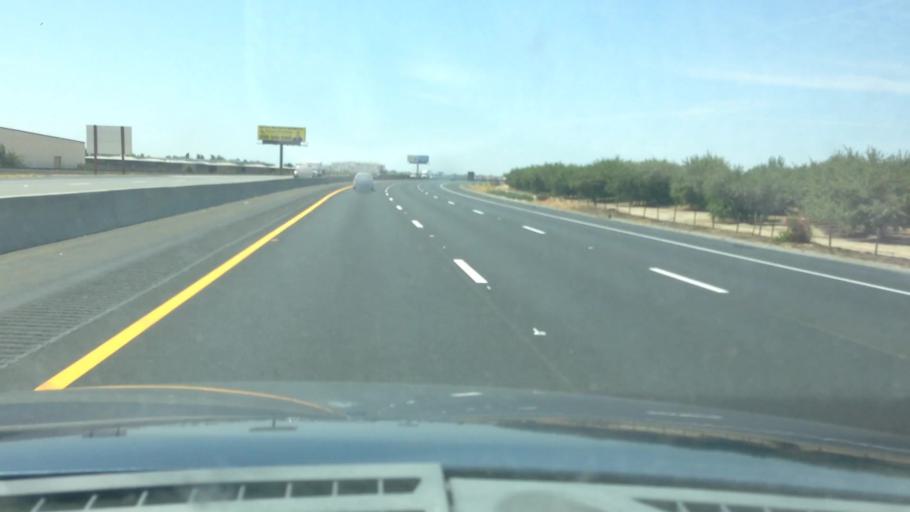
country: US
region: California
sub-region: Kern County
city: McFarland
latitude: 35.7151
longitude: -119.2363
